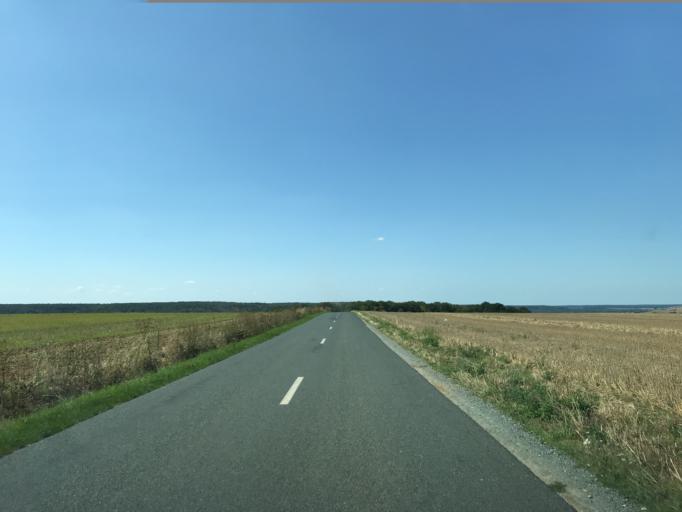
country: FR
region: Haute-Normandie
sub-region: Departement de l'Eure
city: Houlbec-Cocherel
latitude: 49.0828
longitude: 1.3160
